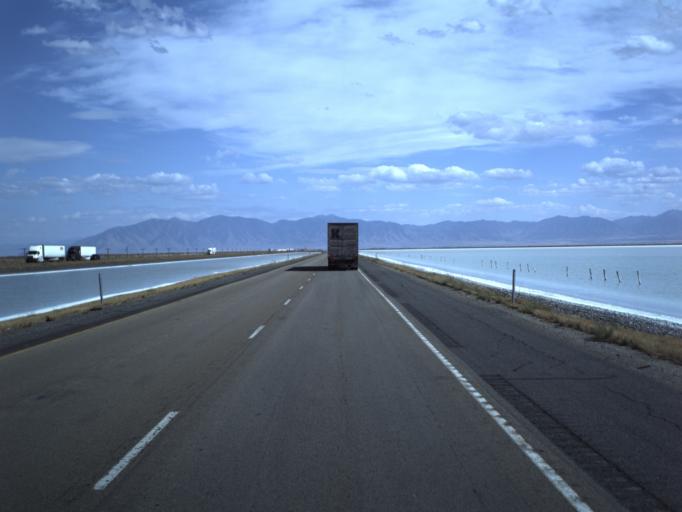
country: US
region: Utah
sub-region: Tooele County
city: Grantsville
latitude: 40.7347
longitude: -112.6056
